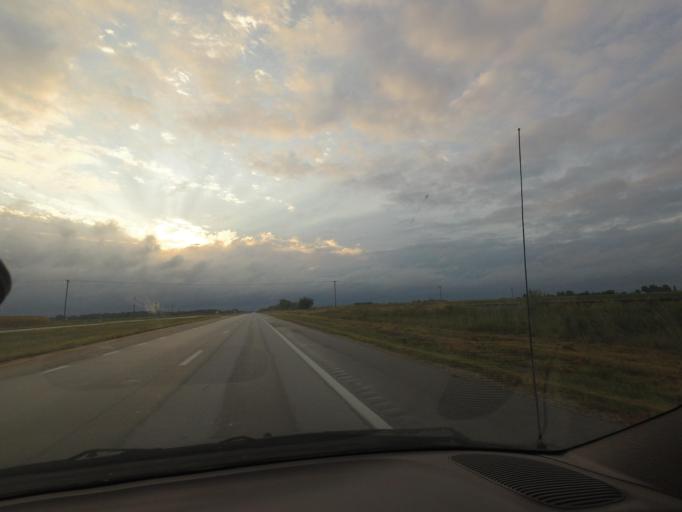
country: US
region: Missouri
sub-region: Shelby County
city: Shelbina
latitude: 39.6841
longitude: -91.9989
